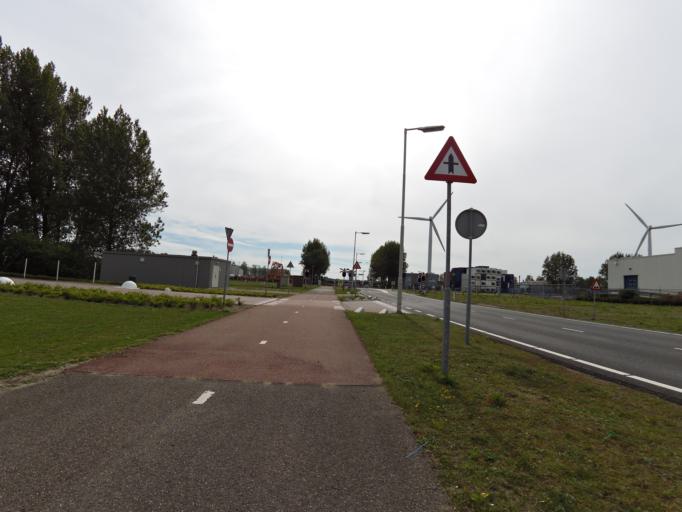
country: NL
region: South Holland
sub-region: Gemeente Brielle
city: Brielle
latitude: 51.9223
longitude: 4.1808
